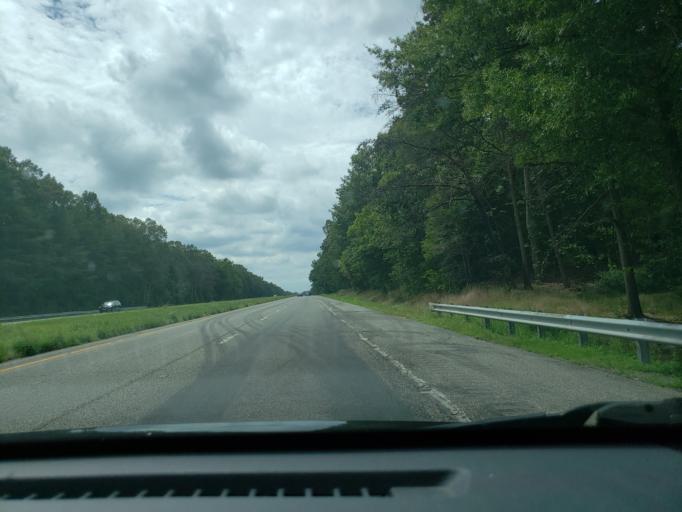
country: US
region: Delaware
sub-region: New Castle County
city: Townsend
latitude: 39.3380
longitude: -75.8351
